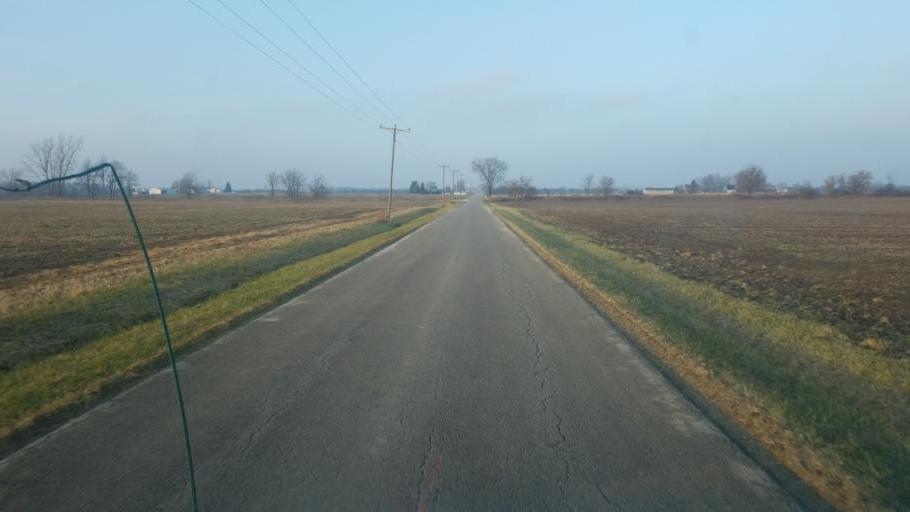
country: US
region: Ohio
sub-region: Wyandot County
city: Carey
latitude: 40.9391
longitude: -83.4290
